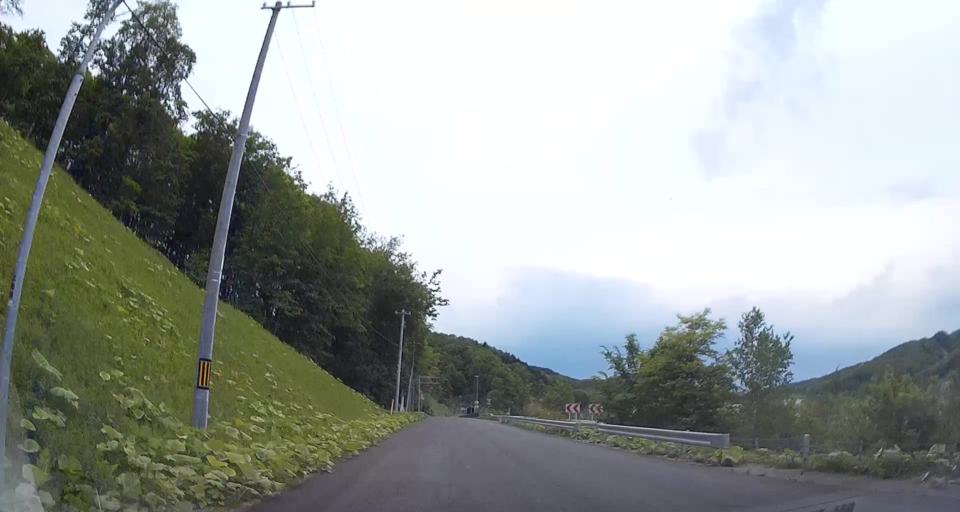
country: JP
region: Hokkaido
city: Chitose
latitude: 42.7728
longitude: 142.0068
